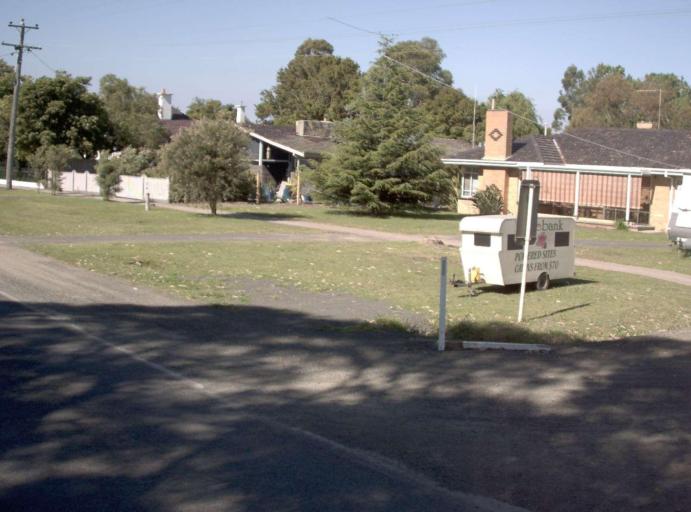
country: AU
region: Victoria
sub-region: Latrobe
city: Traralgon
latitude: -38.5693
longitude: 146.6746
